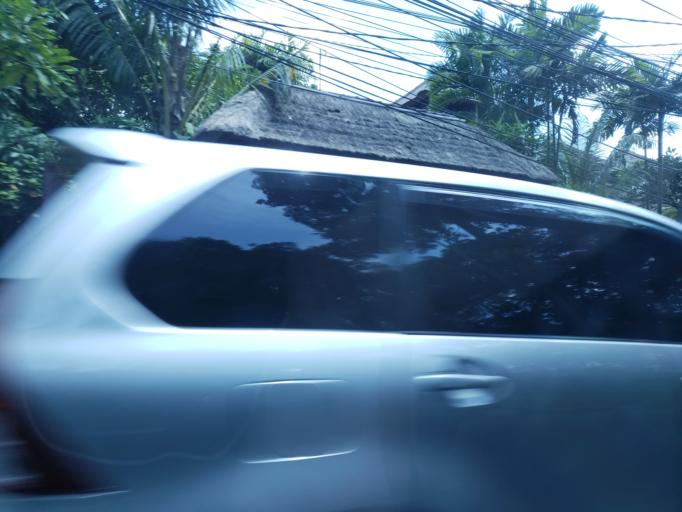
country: ID
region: Bali
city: Jimbaran
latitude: -8.7793
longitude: 115.1684
